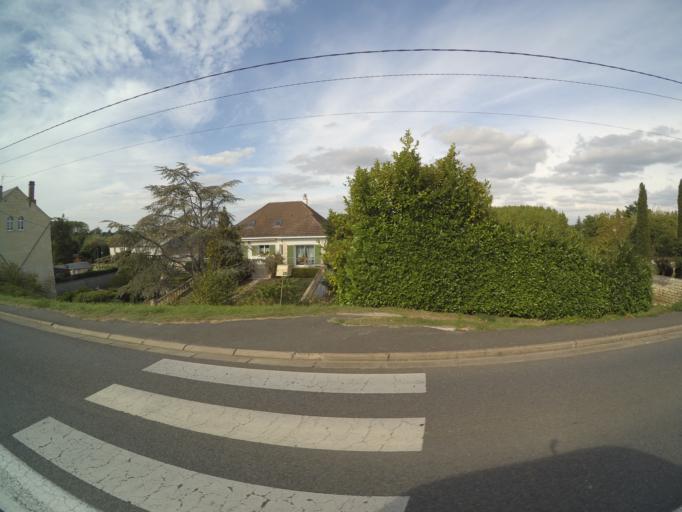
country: FR
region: Centre
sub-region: Departement d'Indre-et-Loire
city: La Chapelle-sur-Loire
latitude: 47.2470
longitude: 0.2177
